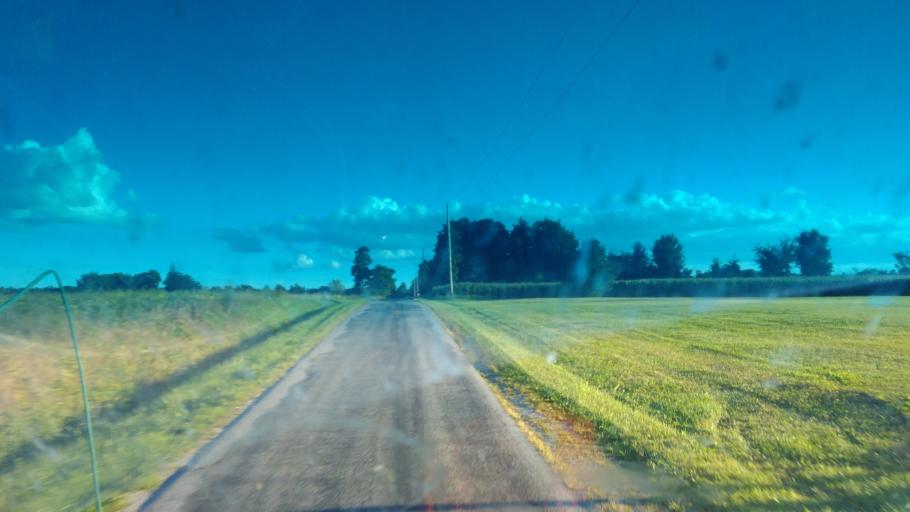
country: US
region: Ohio
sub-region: Wyandot County
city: Upper Sandusky
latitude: 40.8898
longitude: -83.1509
